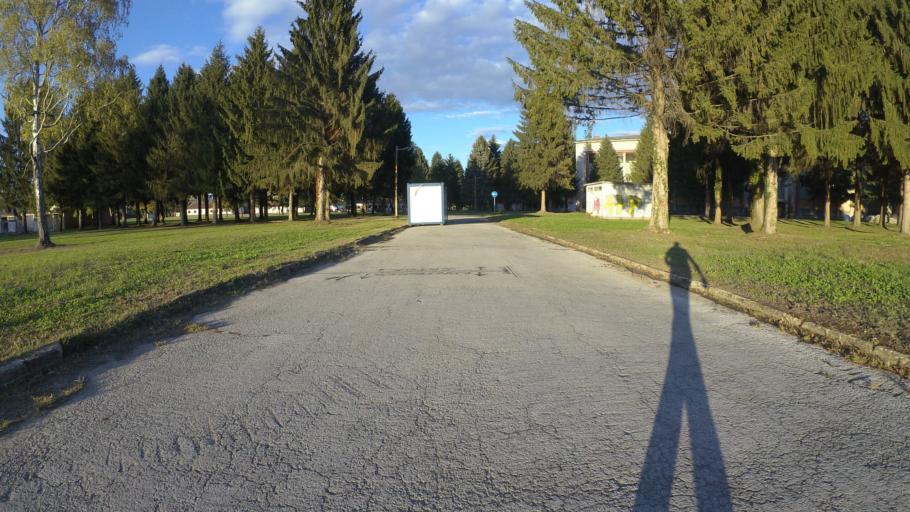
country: HR
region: Karlovacka
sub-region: Grad Karlovac
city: Karlovac
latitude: 45.4838
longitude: 15.5395
